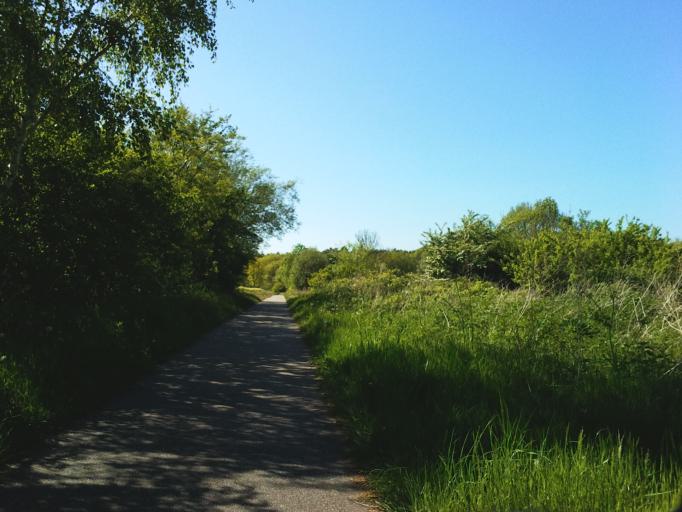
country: DE
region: Mecklenburg-Vorpommern
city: Nienhagen
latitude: 54.1532
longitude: 12.1861
